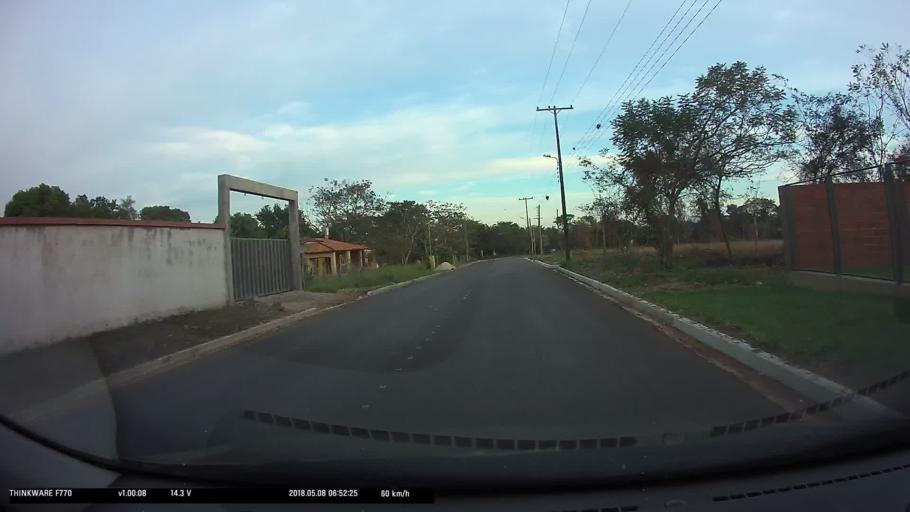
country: PY
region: Central
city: Limpio
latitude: -25.2363
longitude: -57.4658
